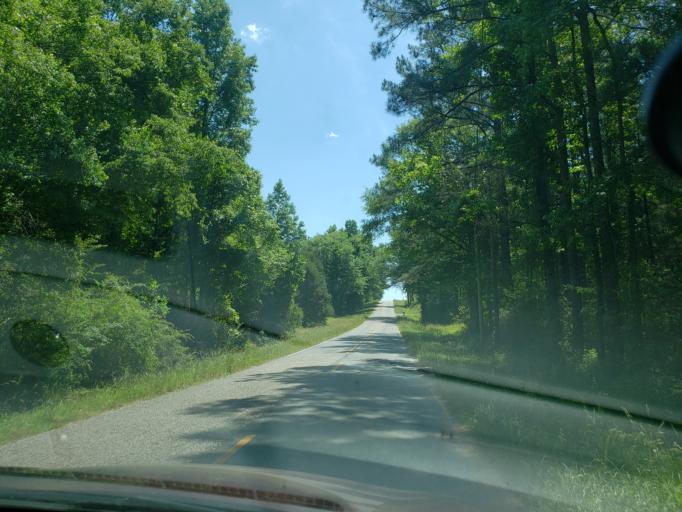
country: US
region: Alabama
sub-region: Elmore County
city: Tallassee
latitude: 32.5809
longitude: -85.8089
